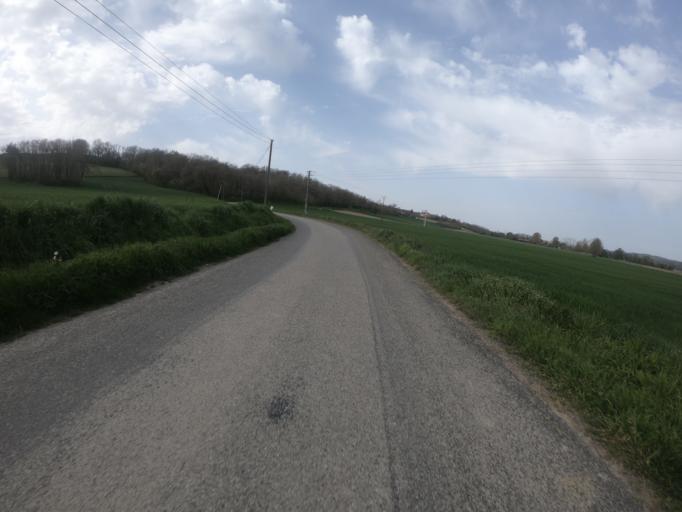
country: FR
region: Midi-Pyrenees
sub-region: Departement de l'Ariege
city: La Tour-du-Crieu
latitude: 43.1337
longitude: 1.7142
